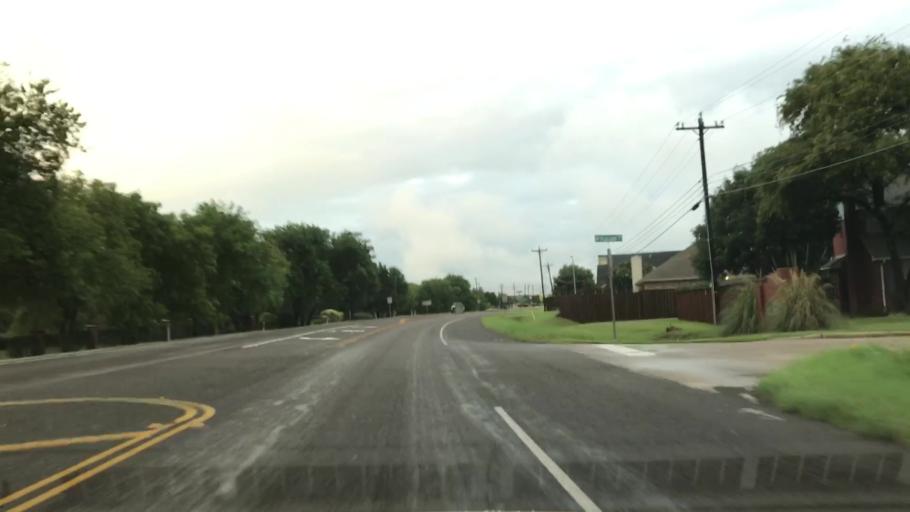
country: US
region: Texas
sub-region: Rockwall County
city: Rockwall
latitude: 32.9695
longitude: -96.4651
